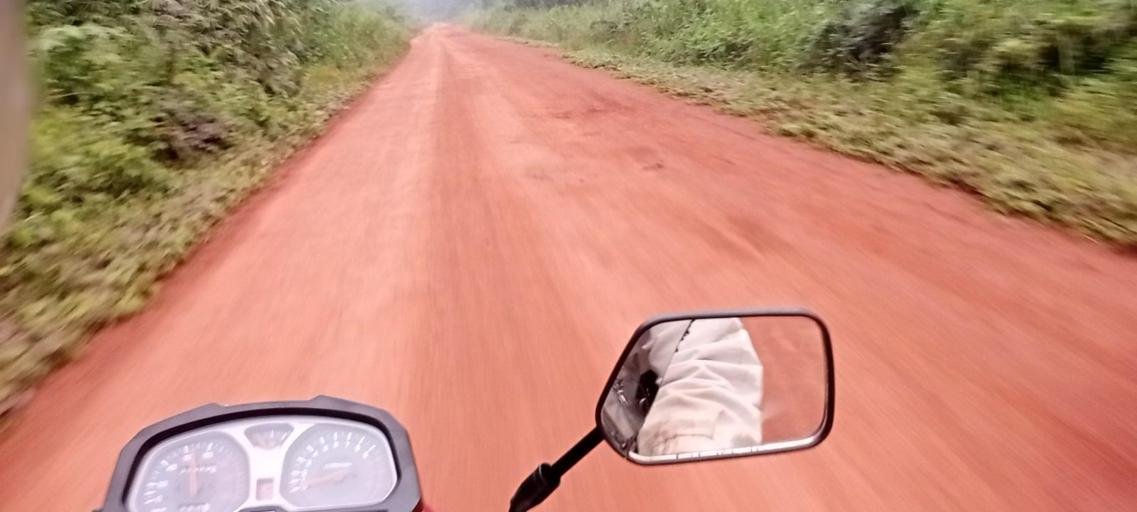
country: CD
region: Eastern Province
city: Kisangani
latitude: -0.0844
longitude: 25.6072
